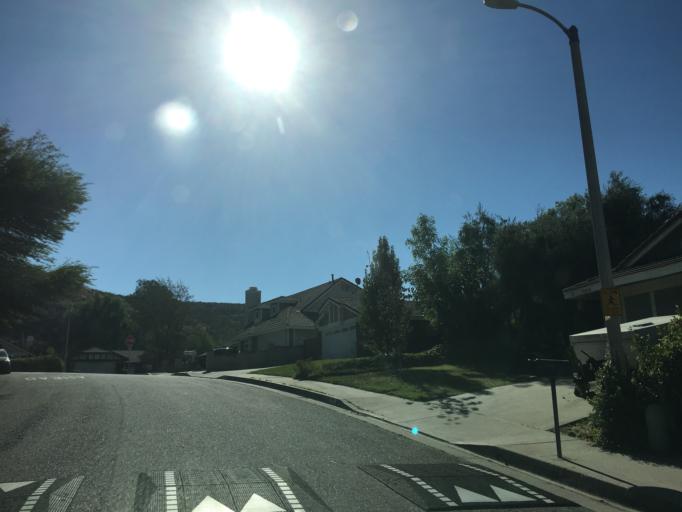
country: US
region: California
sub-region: Los Angeles County
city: Santa Clarita
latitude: 34.4385
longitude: -118.4852
